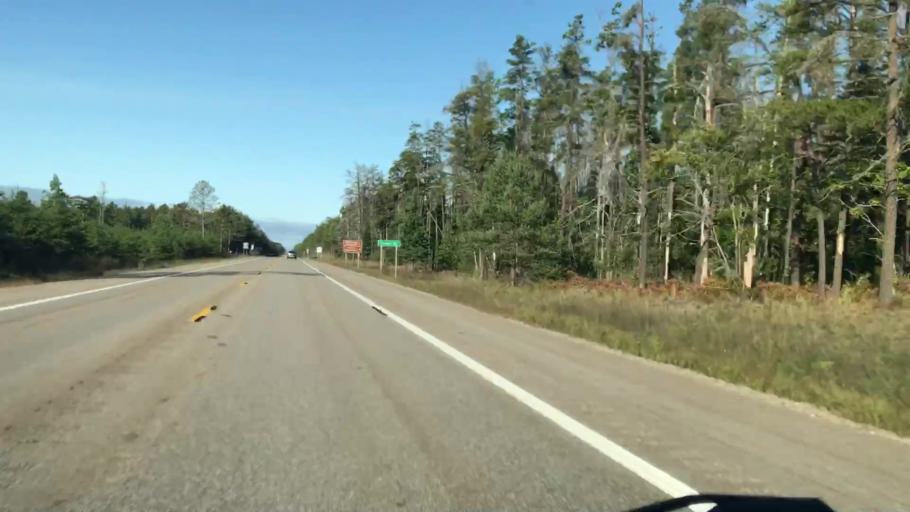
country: US
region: Michigan
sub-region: Chippewa County
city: Sault Ste. Marie
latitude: 46.3701
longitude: -84.7353
